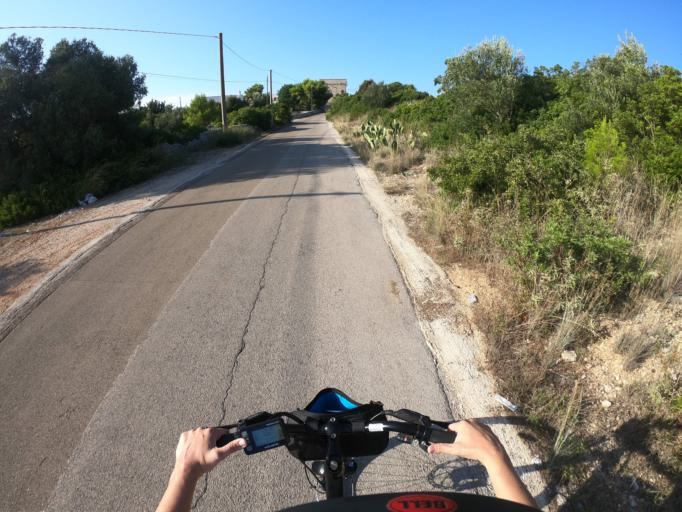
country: IT
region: Apulia
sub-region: Provincia di Lecce
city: Leuca
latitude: 39.8065
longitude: 18.3656
